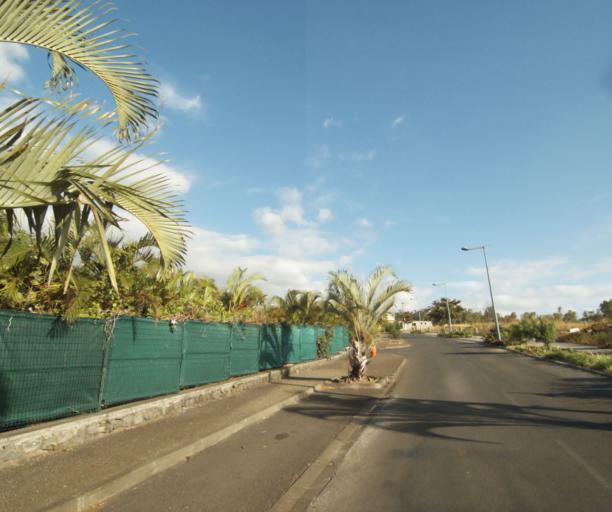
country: RE
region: Reunion
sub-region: Reunion
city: Saint-Paul
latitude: -21.0484
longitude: 55.2600
